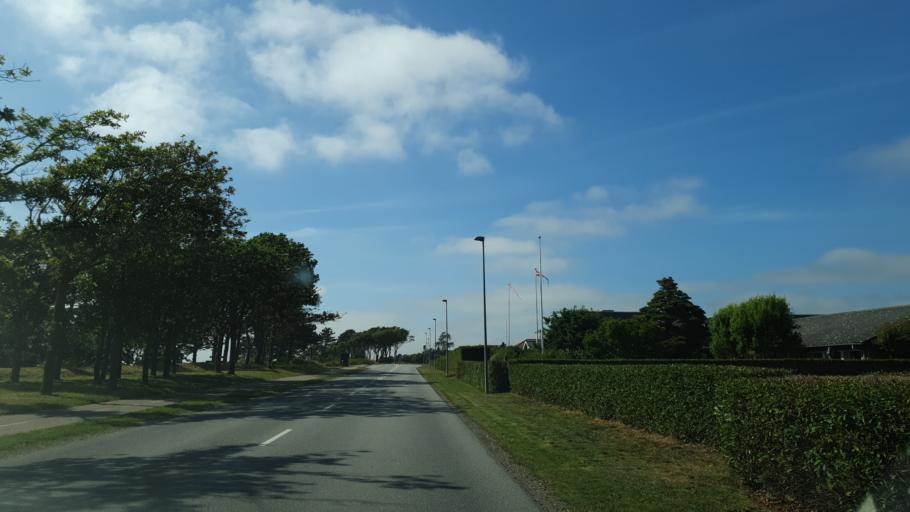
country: DK
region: Central Jutland
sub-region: Ringkobing-Skjern Kommune
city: Ringkobing
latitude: 56.0710
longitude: 8.2757
